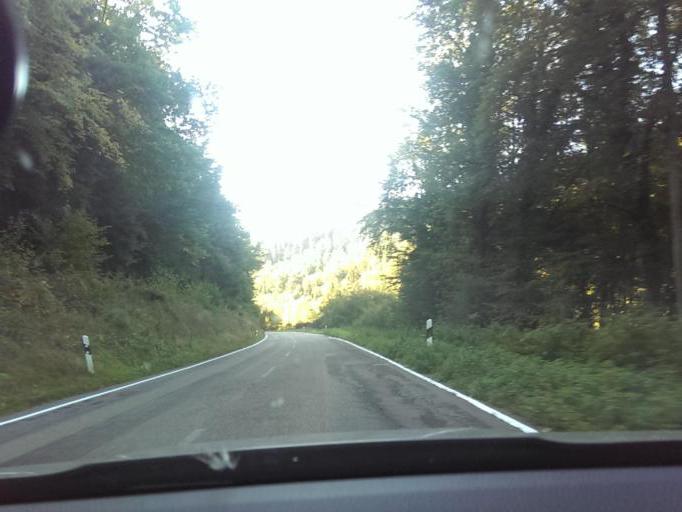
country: DE
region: Baden-Wuerttemberg
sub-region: Karlsruhe Region
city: Tiefenbronn
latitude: 48.8222
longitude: 8.7885
